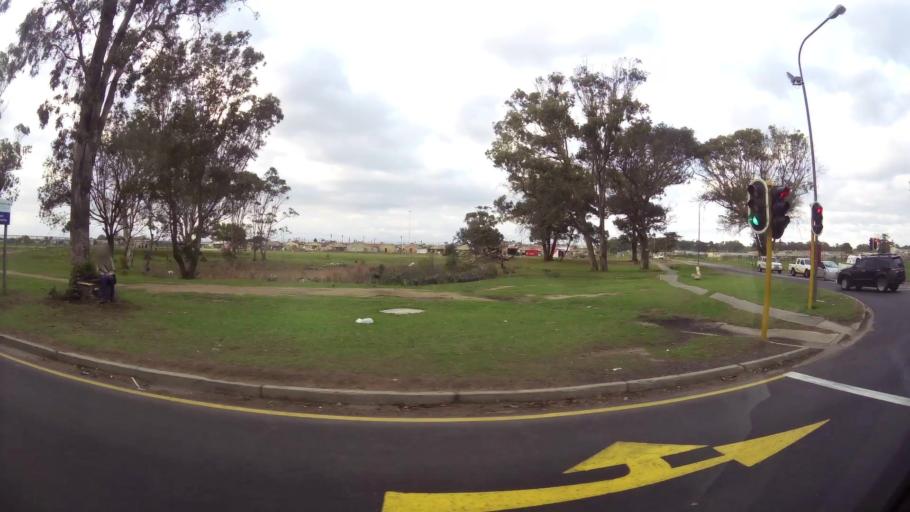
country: ZA
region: Eastern Cape
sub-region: Nelson Mandela Bay Metropolitan Municipality
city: Port Elizabeth
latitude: -33.9851
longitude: 25.5813
